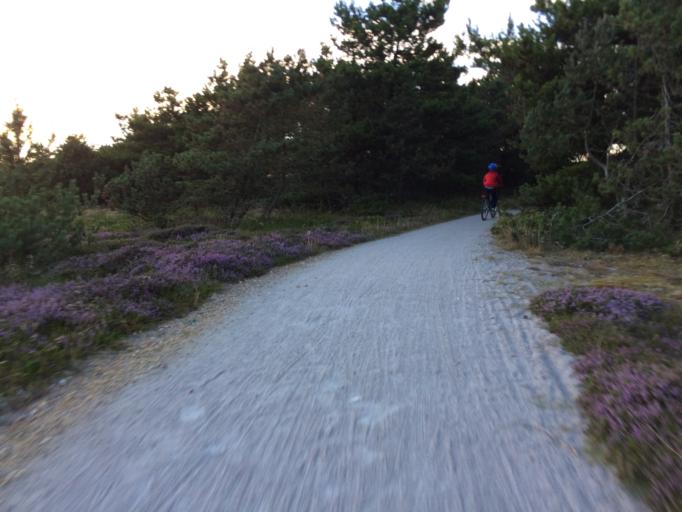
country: DK
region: Central Jutland
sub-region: Ringkobing-Skjern Kommune
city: Hvide Sande
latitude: 55.8765
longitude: 8.1704
